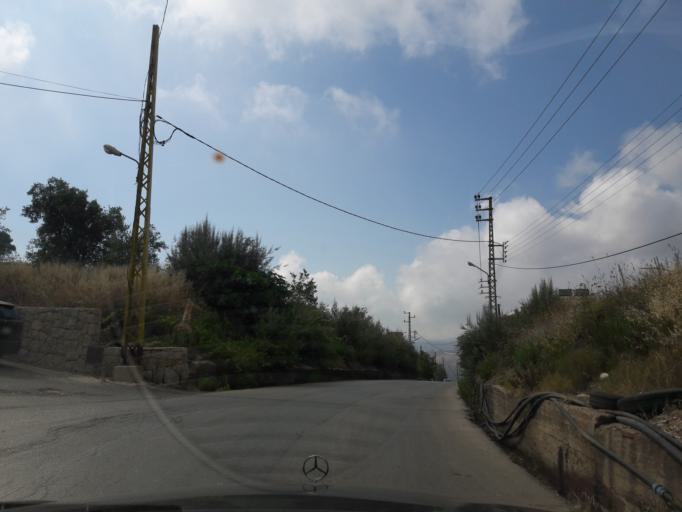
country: LB
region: Beqaa
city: Zahle
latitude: 33.9495
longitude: 35.7793
